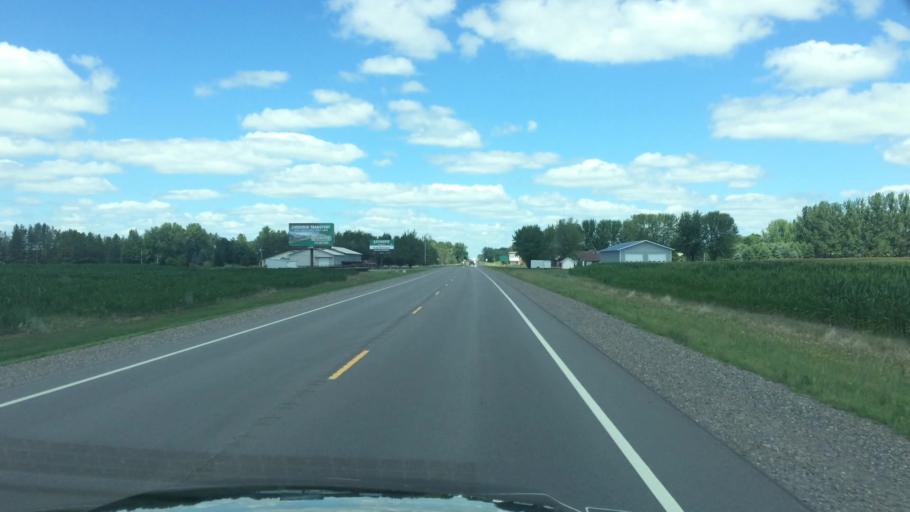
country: US
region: Wisconsin
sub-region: Clark County
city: Abbotsford
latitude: 45.0144
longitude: -90.3152
